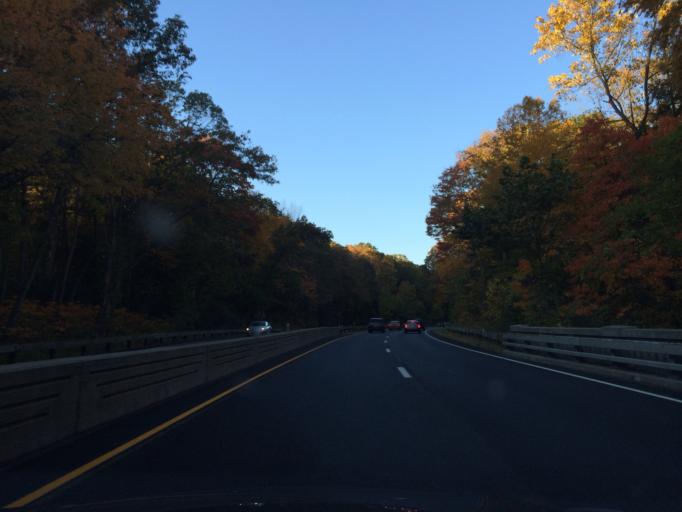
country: US
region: Connecticut
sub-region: Fairfield County
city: Glenville
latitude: 41.0750
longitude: -73.6694
